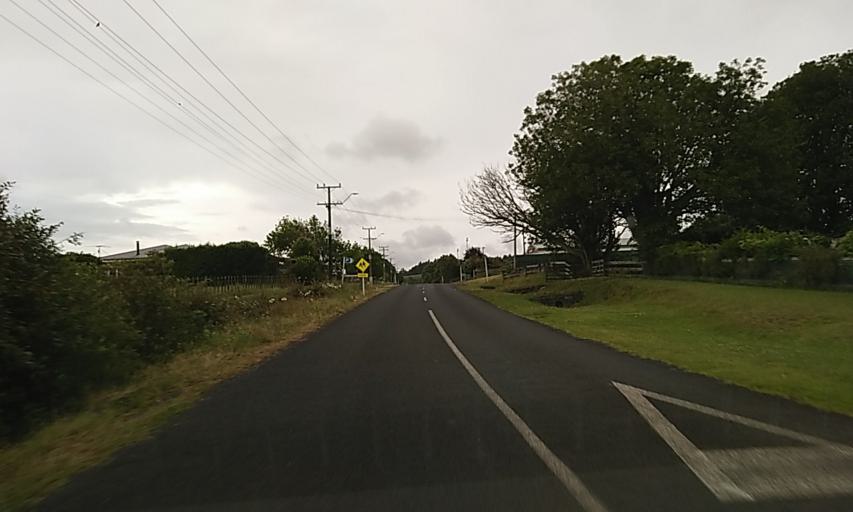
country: NZ
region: Auckland
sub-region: Auckland
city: Pukekohe East
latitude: -37.3289
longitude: 174.9149
